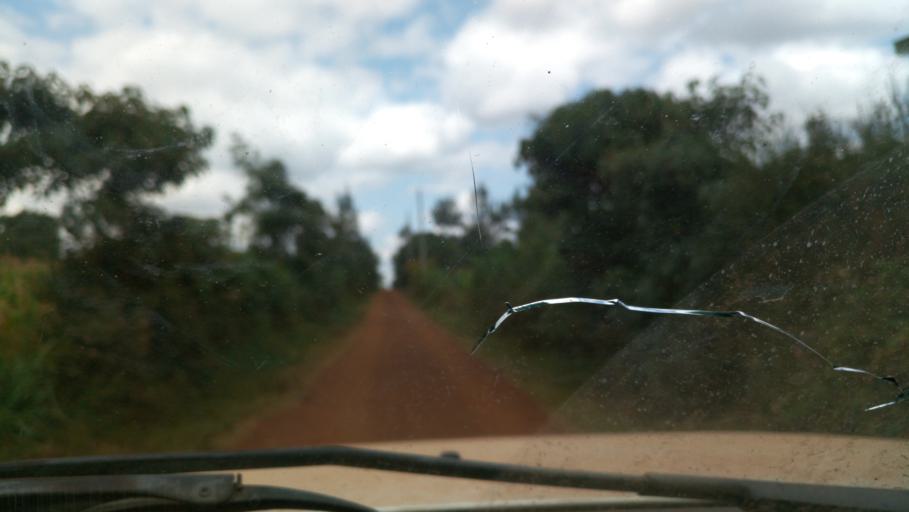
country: KE
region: Nairobi Area
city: Thika
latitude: -0.9534
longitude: 37.0192
